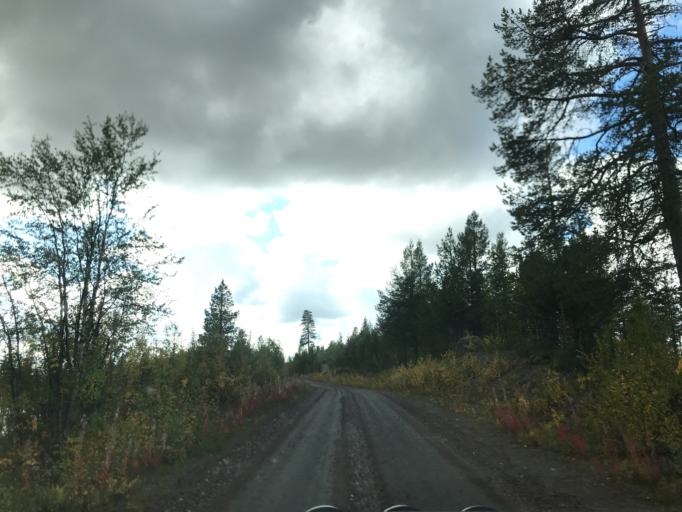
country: SE
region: Norrbotten
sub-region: Gallivare Kommun
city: Malmberget
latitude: 67.5901
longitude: 20.8777
